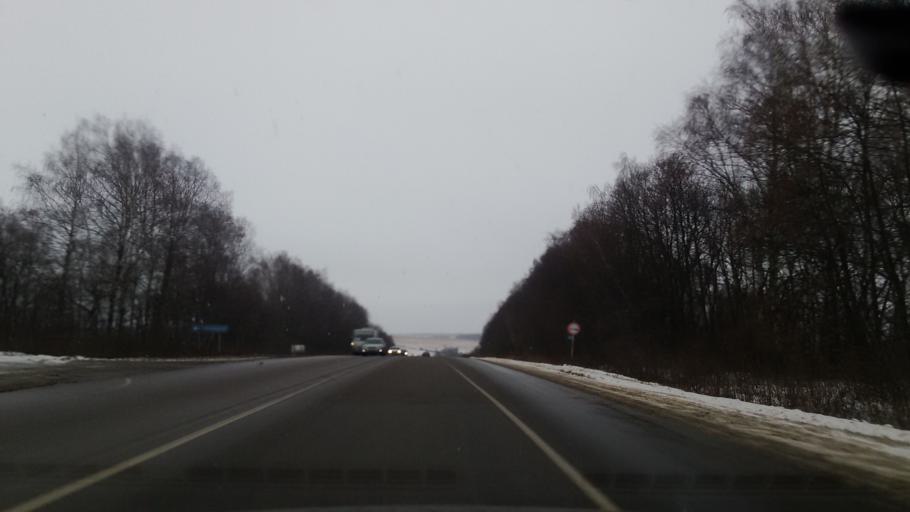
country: RU
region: Tula
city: Bolokhovo
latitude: 54.0417
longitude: 37.8639
